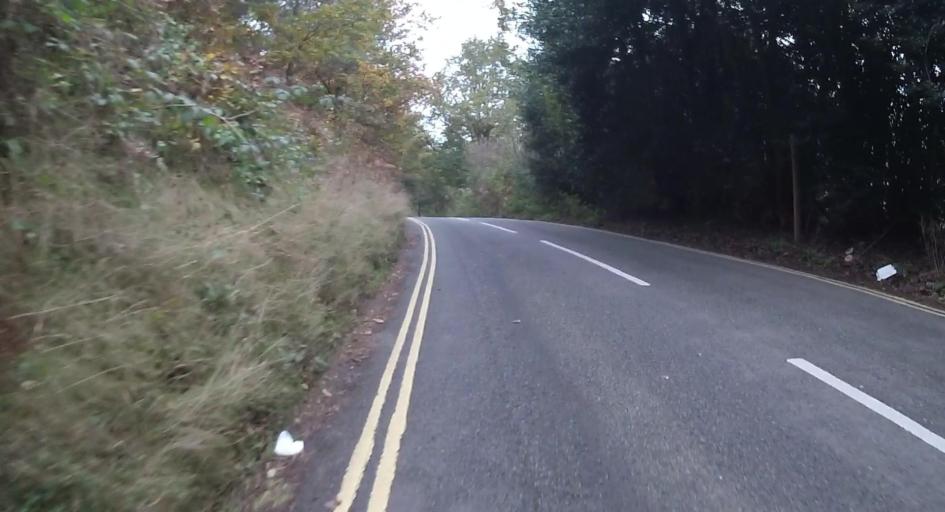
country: GB
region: England
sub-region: Surrey
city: Churt
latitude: 51.1623
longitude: -0.7946
